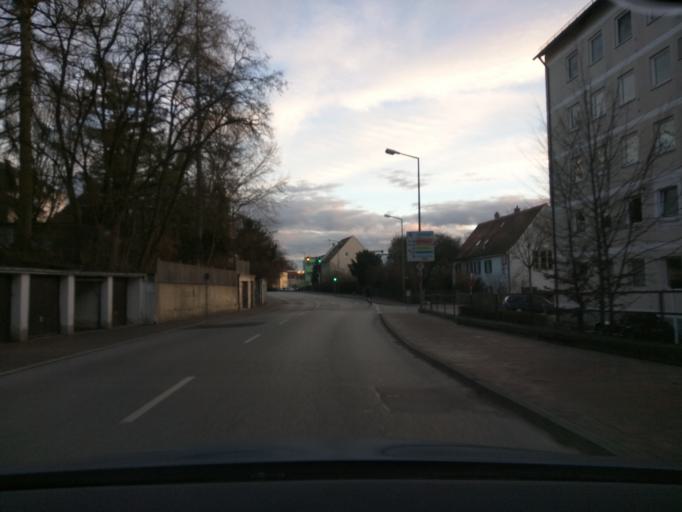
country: DE
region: Bavaria
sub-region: Upper Bavaria
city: Freising
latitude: 48.4010
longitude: 11.7371
